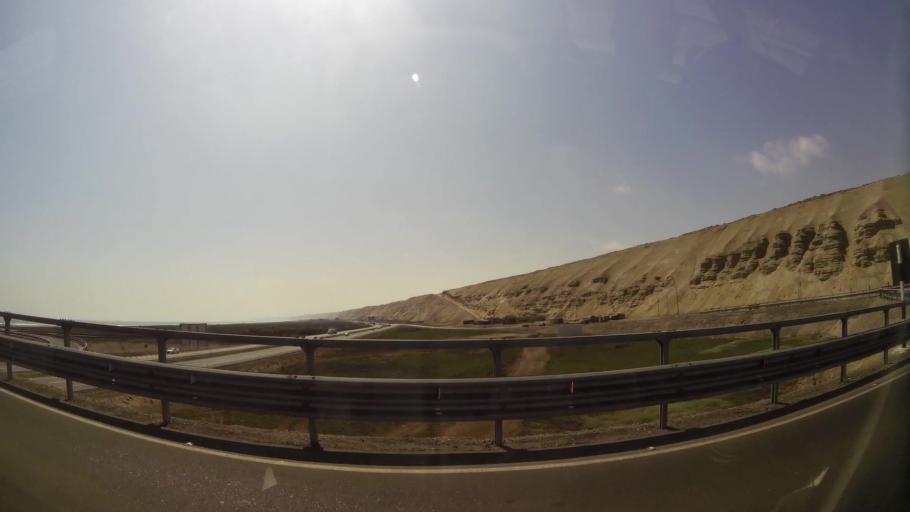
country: PE
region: Ica
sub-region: Provincia de Chincha
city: Sunampe
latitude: -13.4101
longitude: -76.1912
